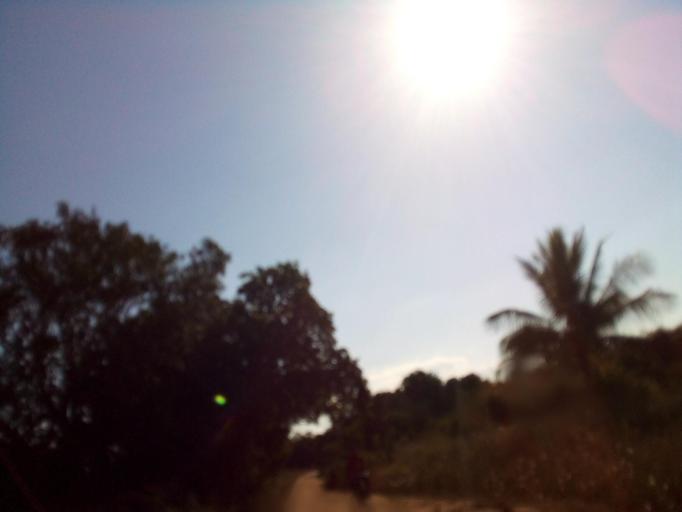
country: MZ
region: Zambezia
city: Quelimane
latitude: -17.5092
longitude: 36.5934
